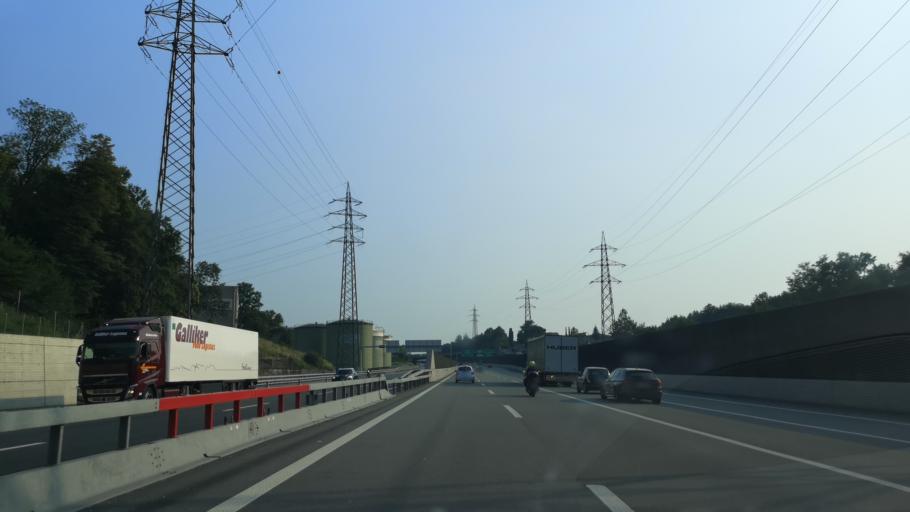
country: CH
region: Ticino
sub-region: Mendrisio District
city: Mendrisio
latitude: 45.8720
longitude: 8.9749
